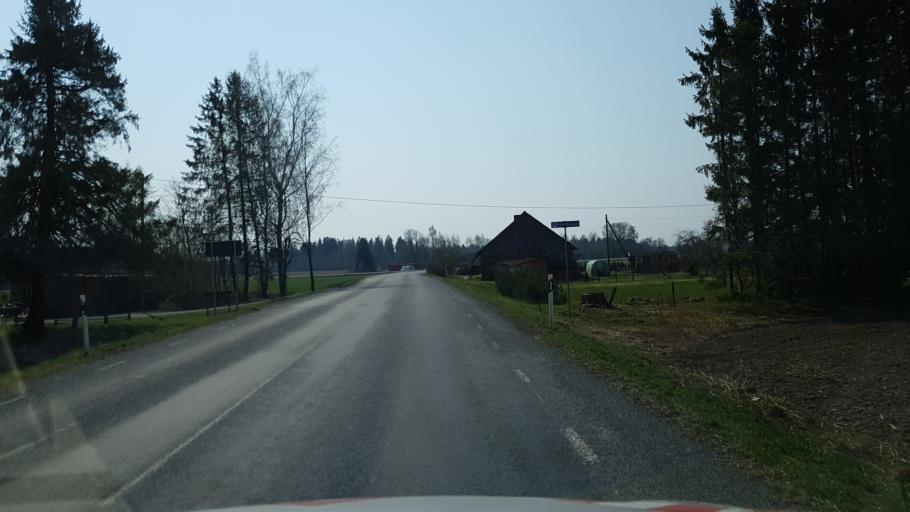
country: EE
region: Raplamaa
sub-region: Kehtna vald
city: Kehtna
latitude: 59.0128
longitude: 24.9201
